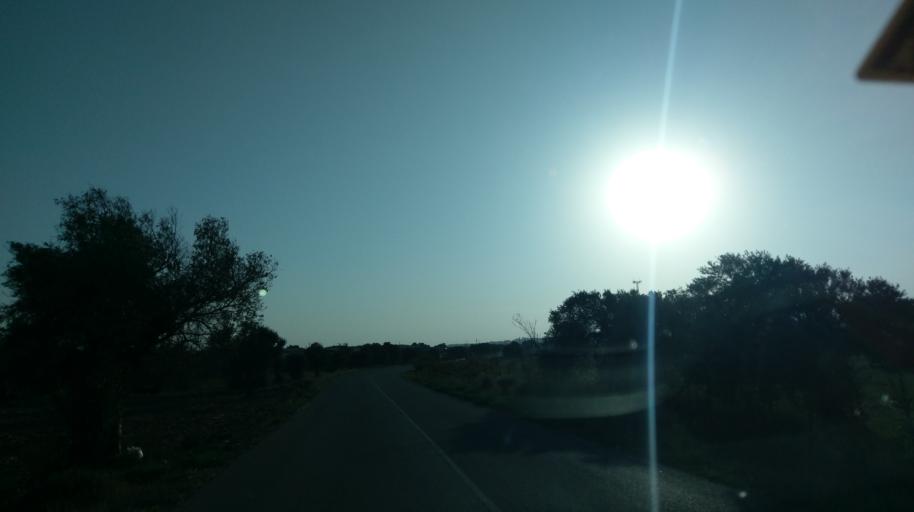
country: CY
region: Ammochostos
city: Leonarisso
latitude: 35.4250
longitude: 34.0100
